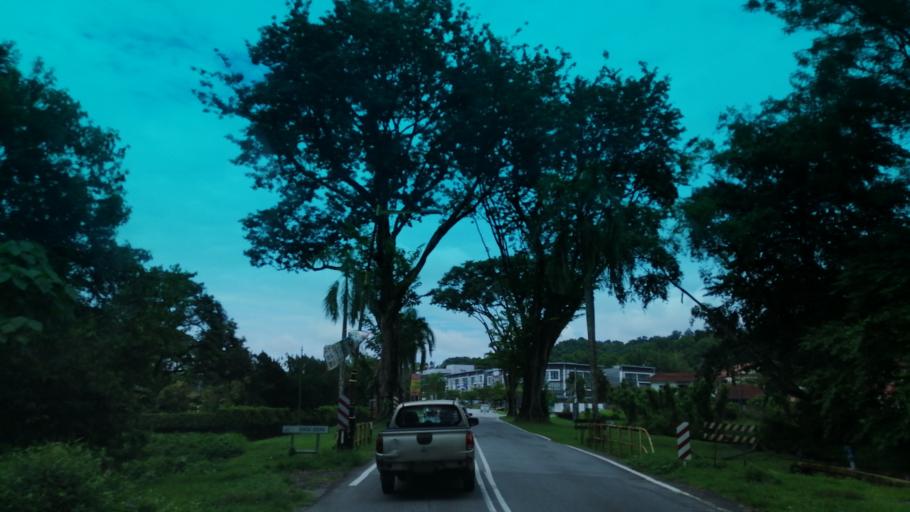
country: MY
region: Perak
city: Taiping
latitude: 4.8589
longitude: 100.7382
